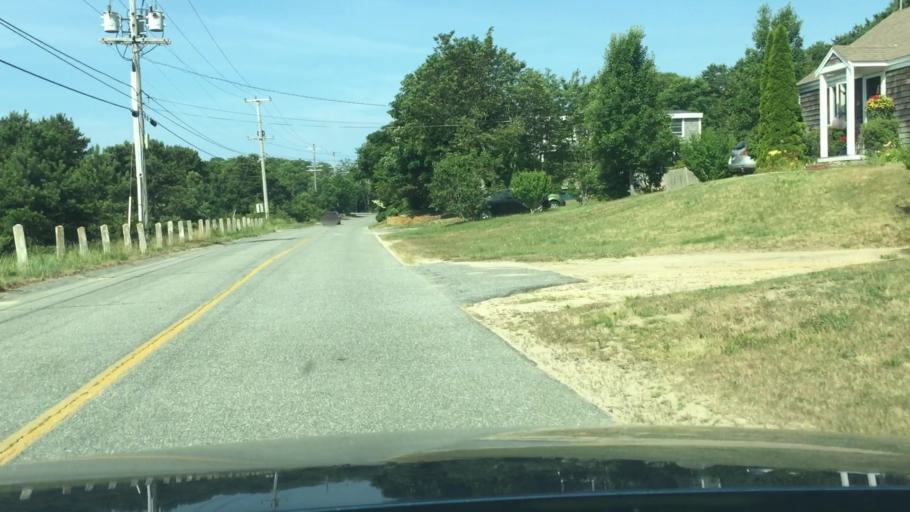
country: US
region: Massachusetts
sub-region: Barnstable County
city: Truro
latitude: 42.0300
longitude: -70.0747
